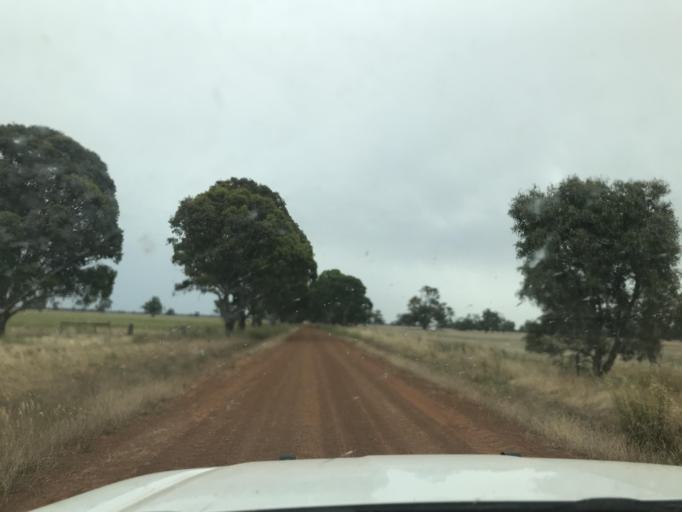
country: AU
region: Victoria
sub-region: Horsham
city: Horsham
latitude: -37.0626
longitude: 141.6317
